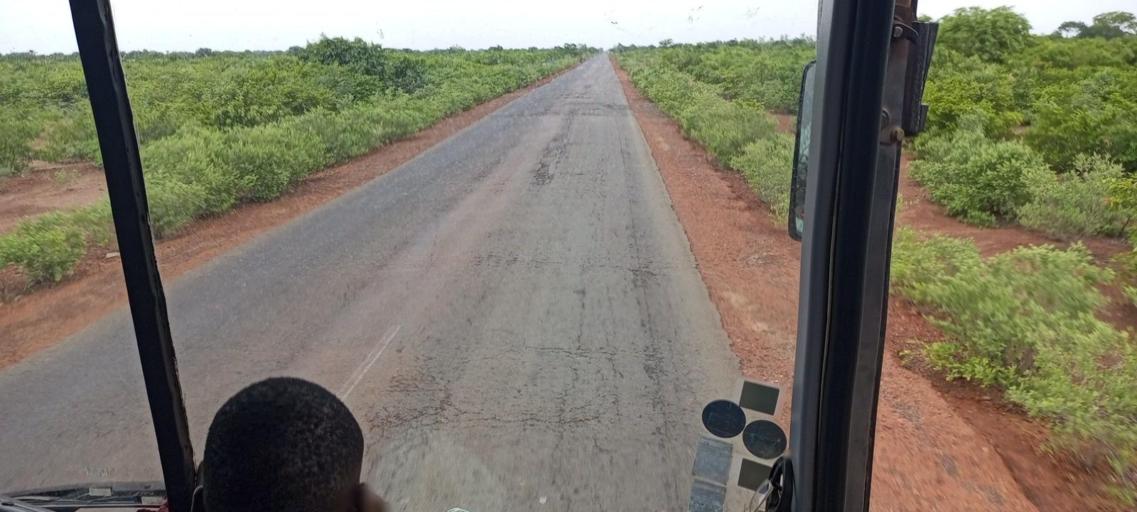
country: ML
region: Sikasso
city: Koutiala
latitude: 12.5520
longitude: -5.5854
